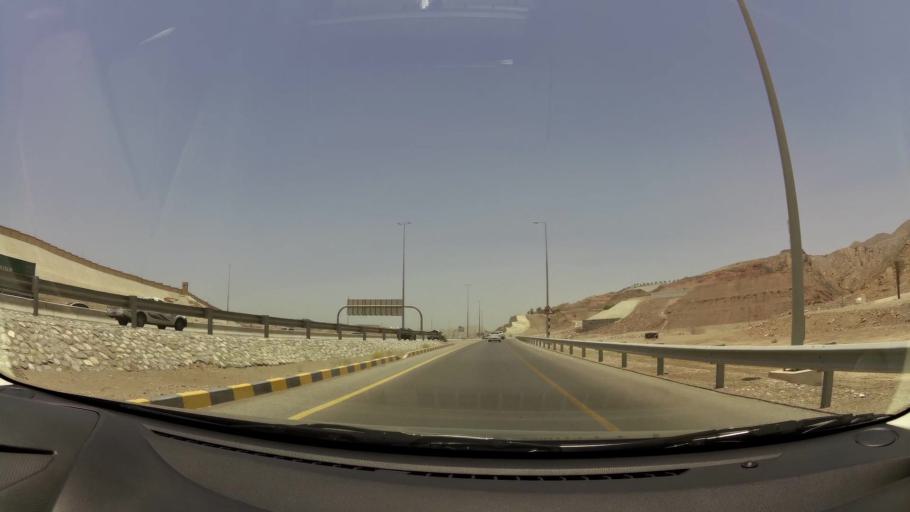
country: OM
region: Muhafazat Masqat
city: Bawshar
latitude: 23.5910
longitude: 58.4650
